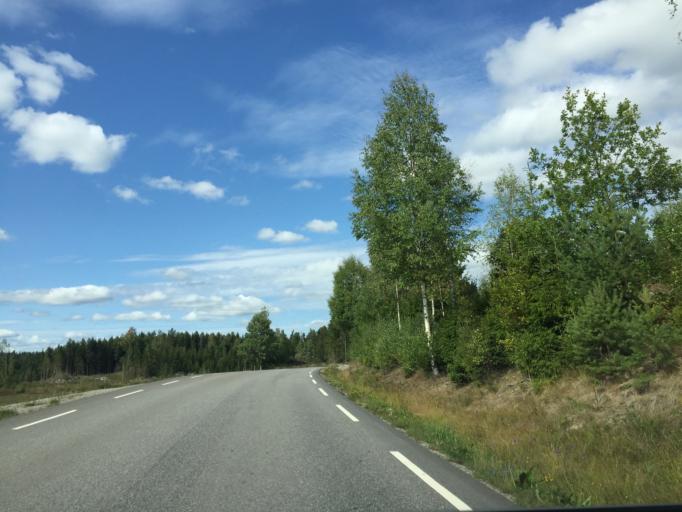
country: NO
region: Ostfold
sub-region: Hobol
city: Elvestad
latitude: 59.6051
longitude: 10.9044
